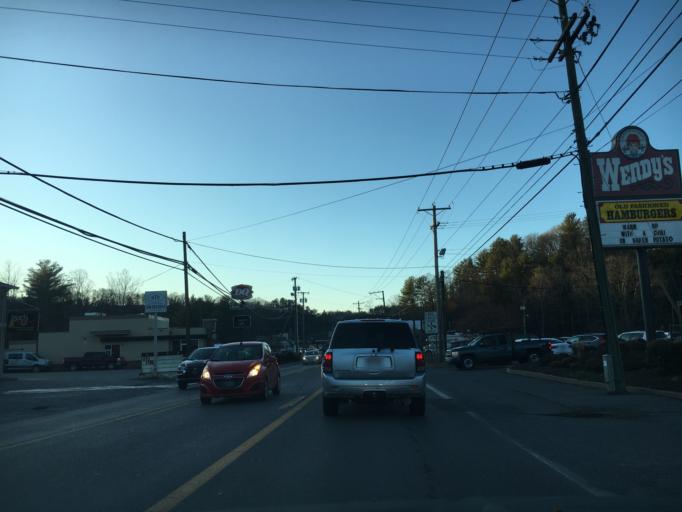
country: US
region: West Virginia
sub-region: Raleigh County
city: Beaver
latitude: 37.7495
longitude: -81.1378
